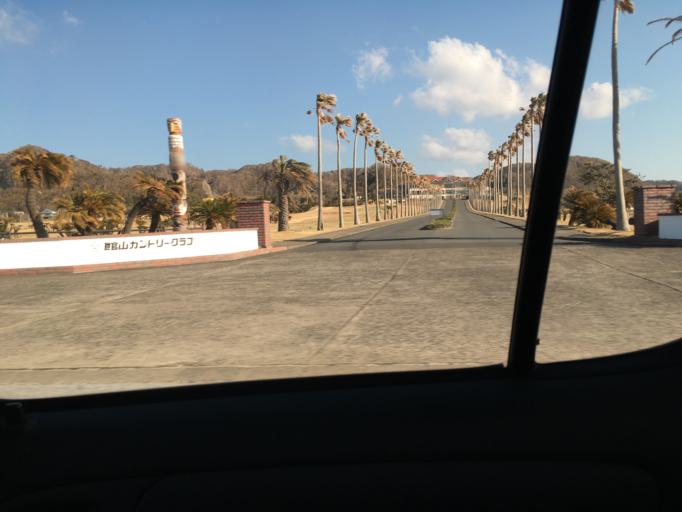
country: JP
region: Chiba
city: Tateyama
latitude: 34.9484
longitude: 139.8084
